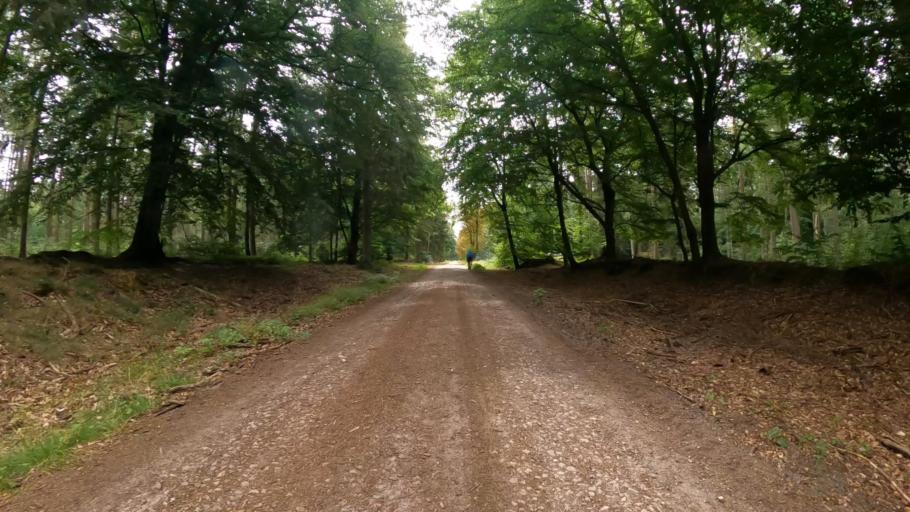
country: DE
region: Schleswig-Holstein
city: Bark
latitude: 53.9467
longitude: 10.1428
